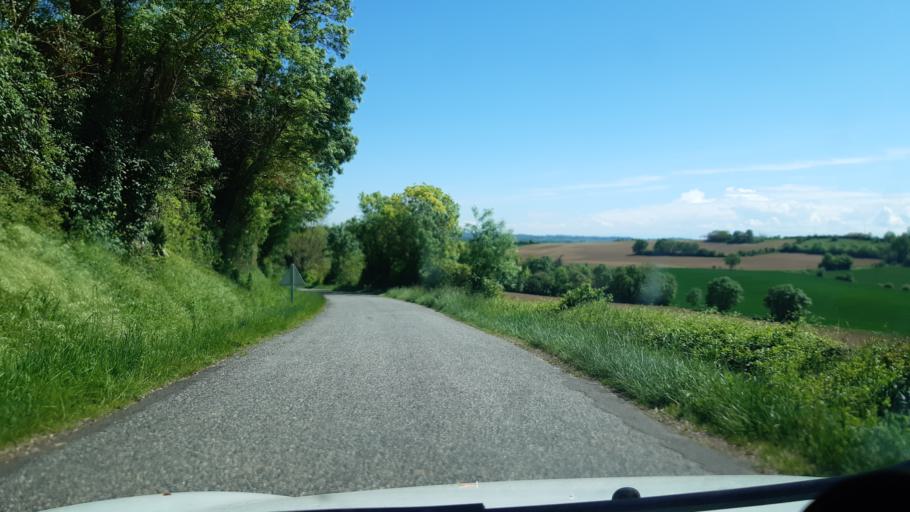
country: FR
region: Midi-Pyrenees
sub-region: Departement du Gers
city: Samatan
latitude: 43.5112
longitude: 1.0110
